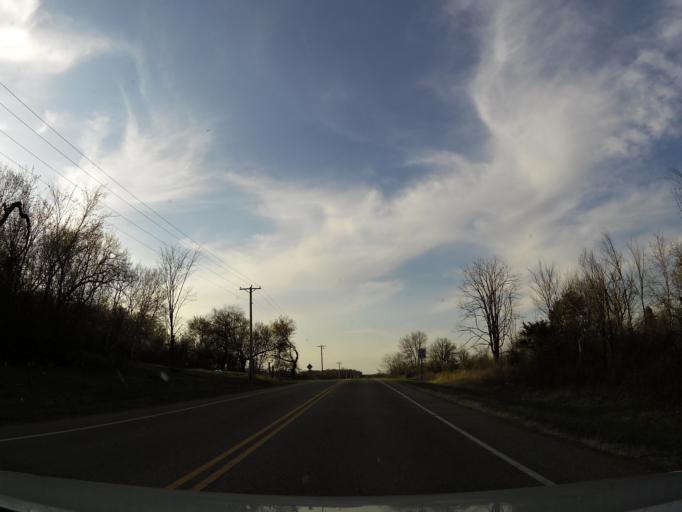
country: US
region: Wisconsin
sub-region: Pierce County
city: River Falls
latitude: 44.8943
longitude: -92.6700
